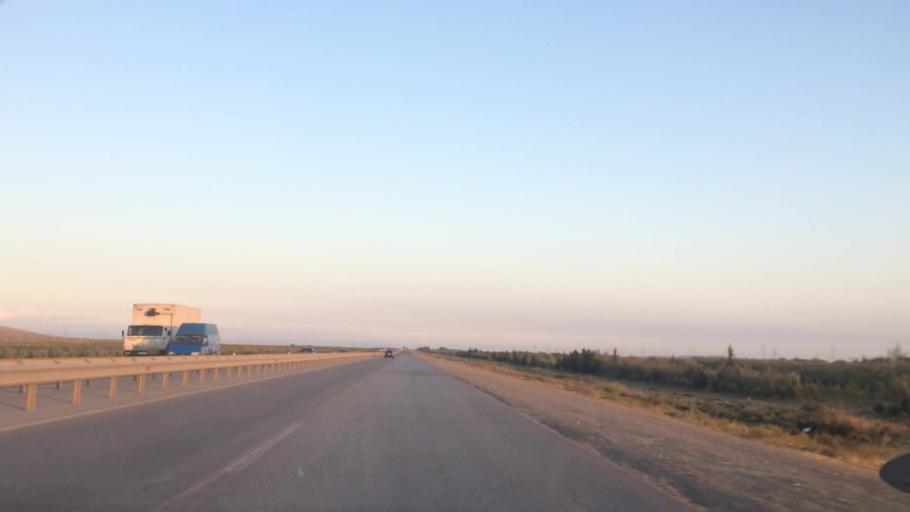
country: AZ
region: Baki
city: Qobustan
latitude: 39.9609
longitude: 49.2931
